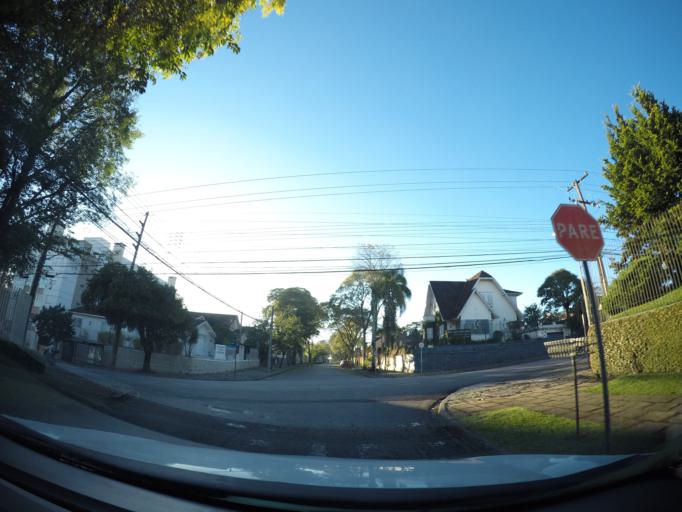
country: BR
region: Parana
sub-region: Curitiba
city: Curitiba
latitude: -25.4174
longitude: -49.2809
